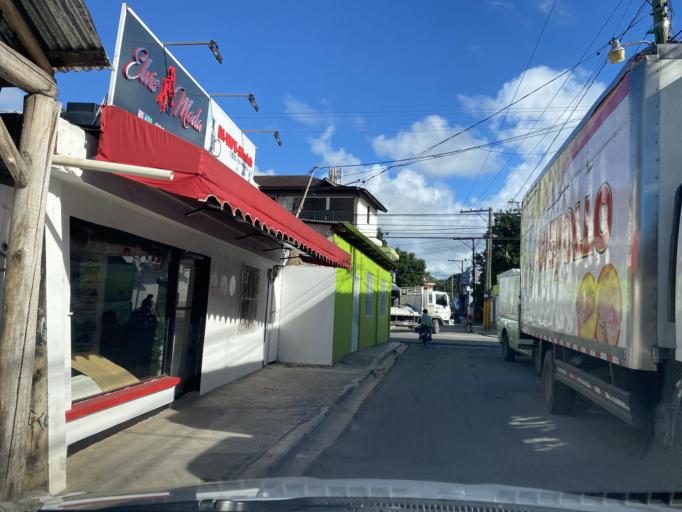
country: DO
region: Samana
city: Las Terrenas
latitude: 19.3136
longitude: -69.5427
